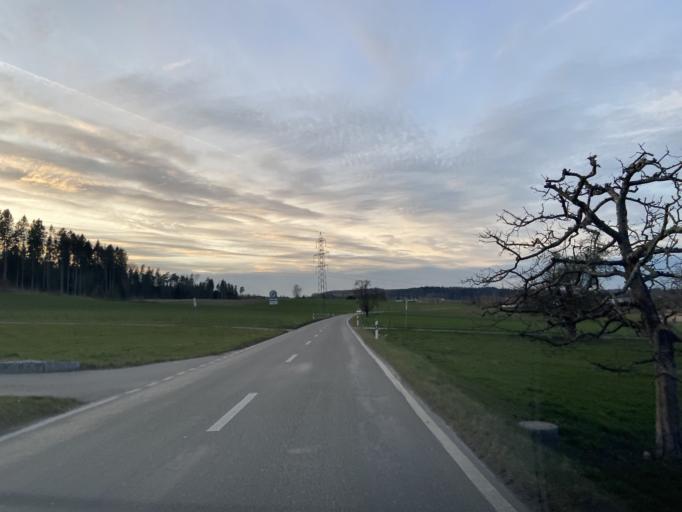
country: CH
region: Zurich
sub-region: Bezirk Winterthur
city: Wuelflingen (Kreis 6) / Haerti
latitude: 47.5294
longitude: 8.6915
